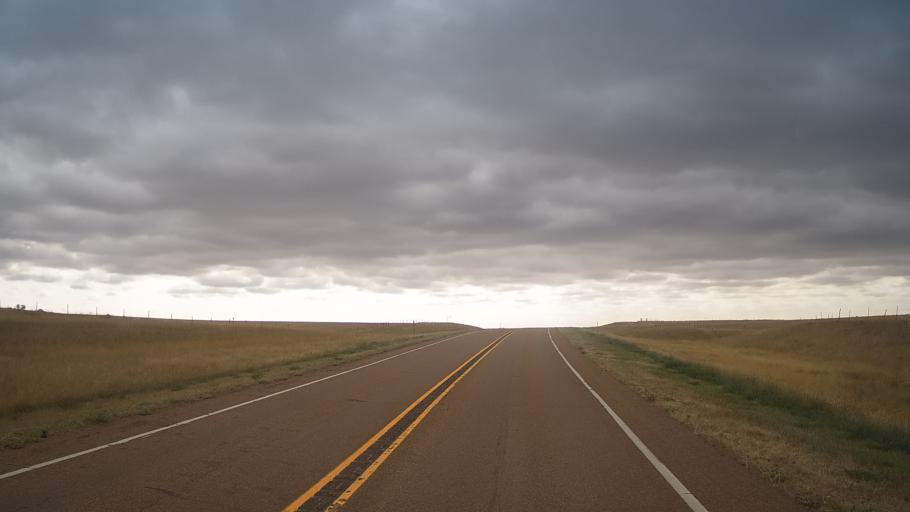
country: US
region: Montana
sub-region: Valley County
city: Glasgow
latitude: 48.3683
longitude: -106.7905
